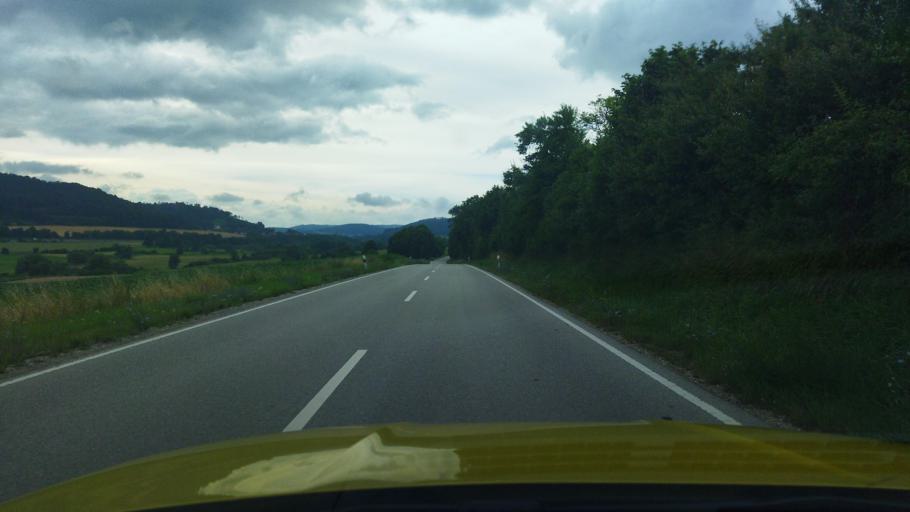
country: DE
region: Bavaria
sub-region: Regierungsbezirk Mittelfranken
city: Greding
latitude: 49.0487
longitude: 11.3448
